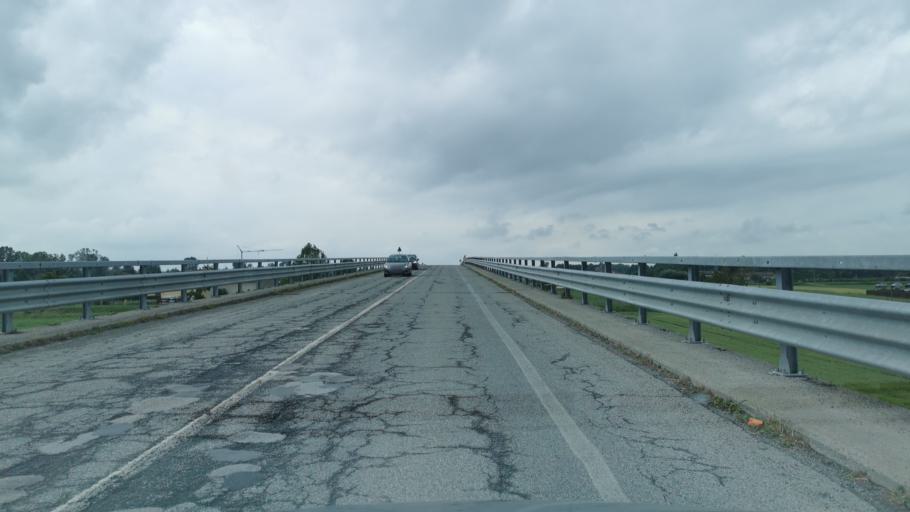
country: IT
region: Piedmont
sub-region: Provincia di Cuneo
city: Savigliano
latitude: 44.6385
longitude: 7.6427
